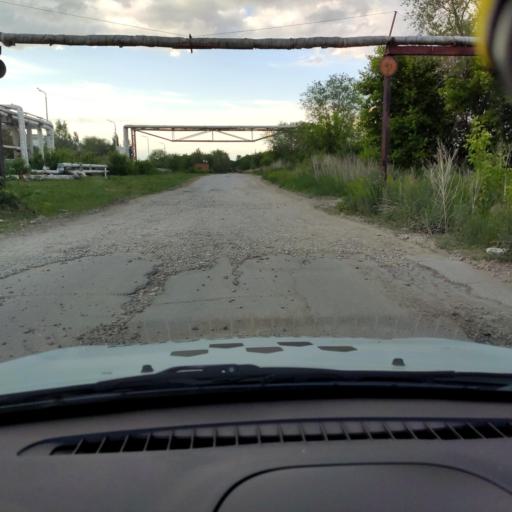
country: RU
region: Samara
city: Podstepki
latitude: 53.5807
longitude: 49.2289
